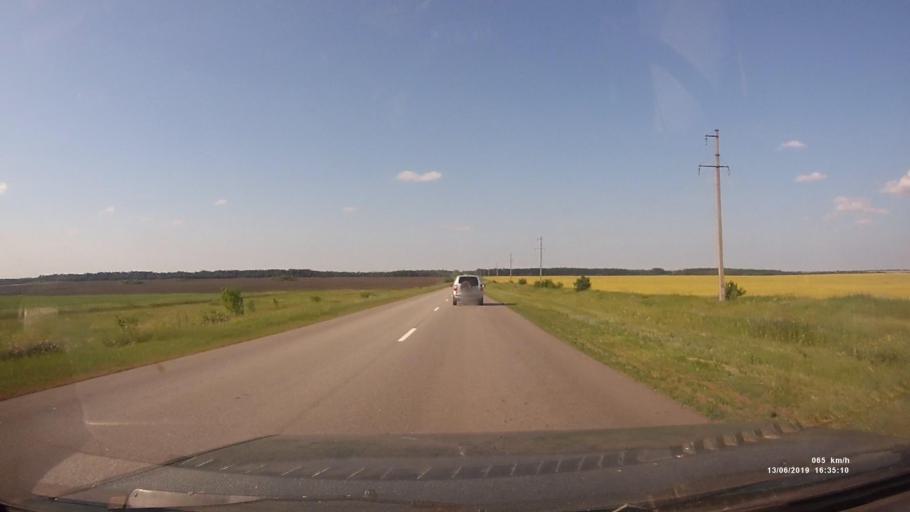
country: RU
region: Rostov
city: Kazanskaya
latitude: 49.8798
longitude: 41.2969
